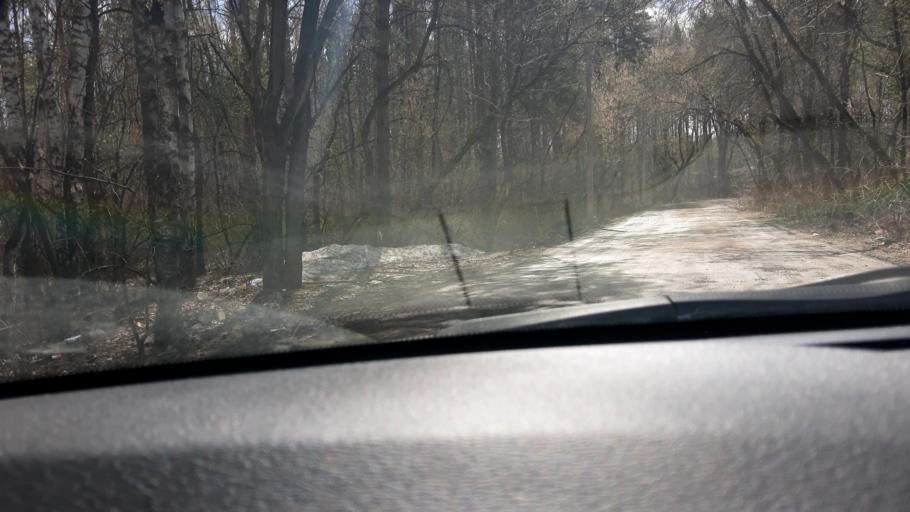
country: RU
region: Bashkortostan
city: Ufa
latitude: 54.6983
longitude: 55.9331
